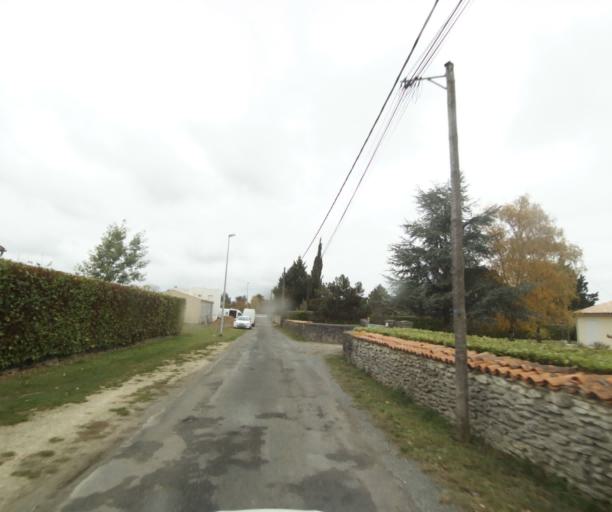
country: FR
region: Poitou-Charentes
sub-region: Departement de la Charente-Maritime
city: Bussac-sur-Charente
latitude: 45.7684
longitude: -0.6322
